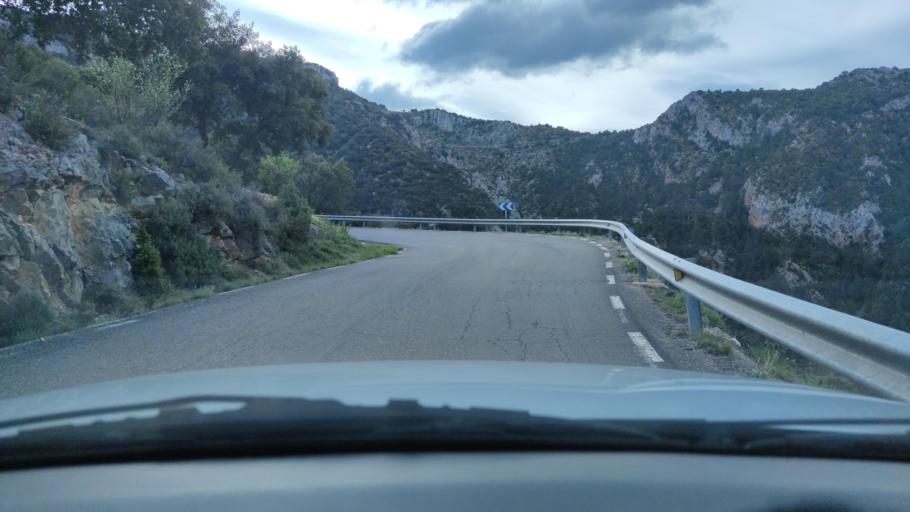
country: ES
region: Catalonia
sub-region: Provincia de Lleida
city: Coll de Nargo
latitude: 42.2472
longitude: 1.3579
